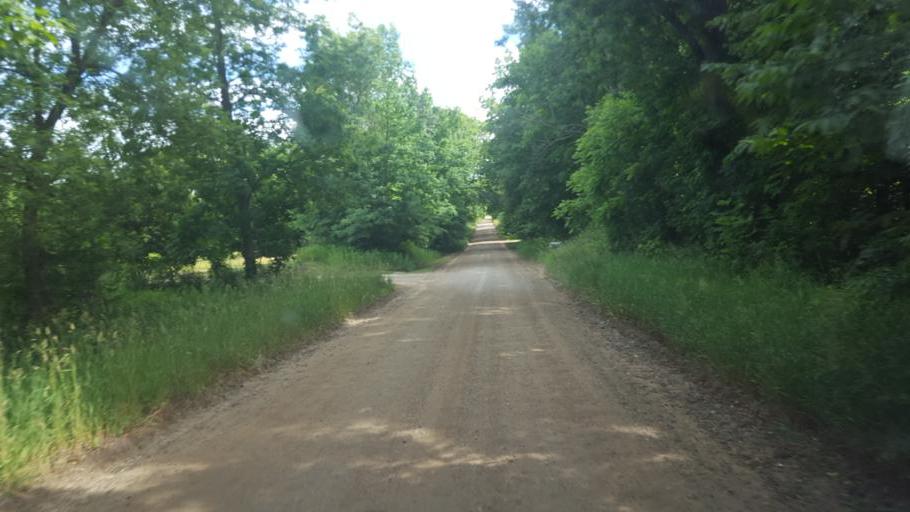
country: US
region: Michigan
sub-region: Barry County
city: Nashville
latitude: 42.5920
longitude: -84.9753
